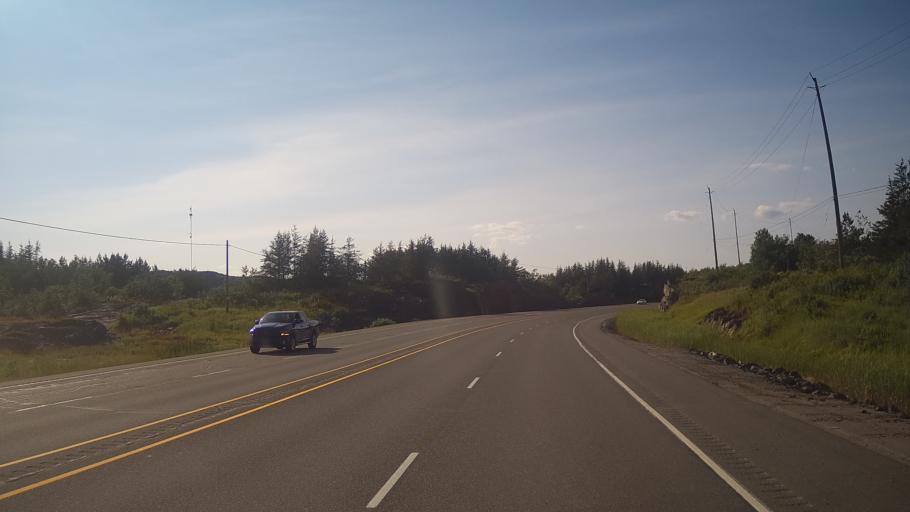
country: CA
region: Ontario
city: Greater Sudbury
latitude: 46.5079
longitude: -81.0501
